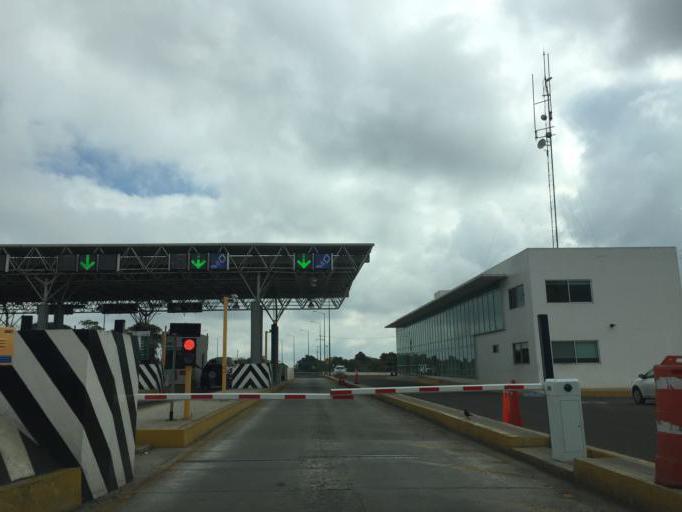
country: MX
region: Puebla
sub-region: Pantepec
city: Ameluca
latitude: 20.4585
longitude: -97.8542
